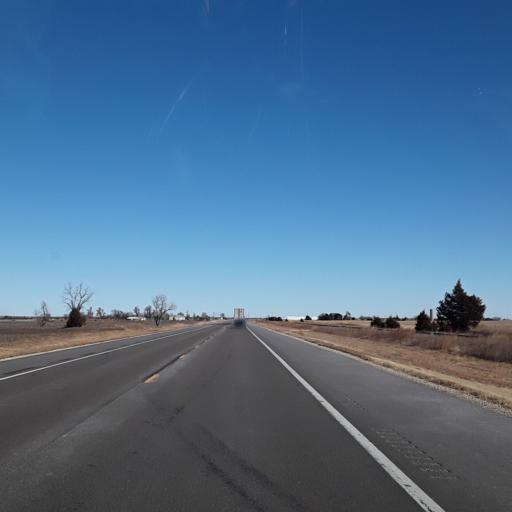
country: US
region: Kansas
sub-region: Pawnee County
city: Larned
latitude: 38.1943
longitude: -99.0771
